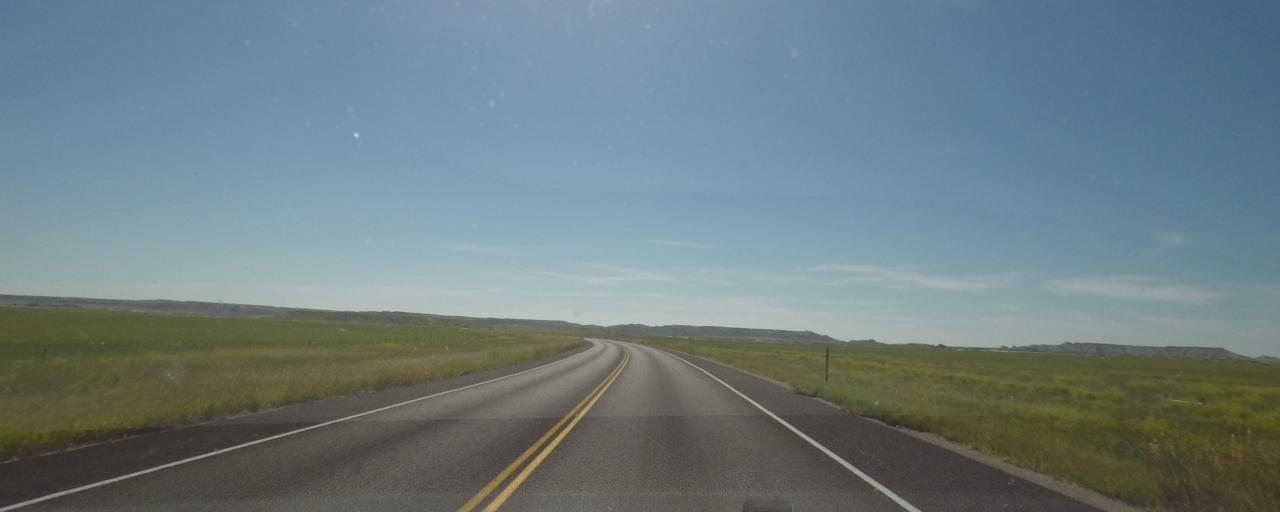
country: US
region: South Dakota
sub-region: Shannon County
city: Porcupine
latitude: 43.7794
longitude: -102.5473
